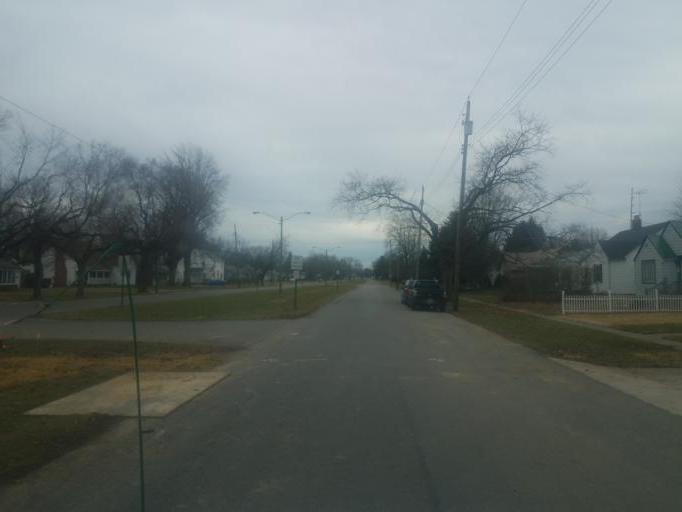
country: US
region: Ohio
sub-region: Marion County
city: Marion
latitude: 40.5872
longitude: -83.1065
